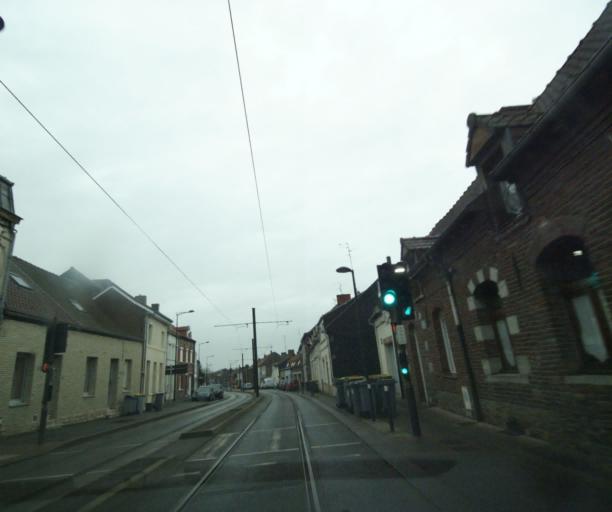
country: FR
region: Nord-Pas-de-Calais
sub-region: Departement du Nord
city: Fresnes-sur-Escaut
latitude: 50.4340
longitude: 3.5802
